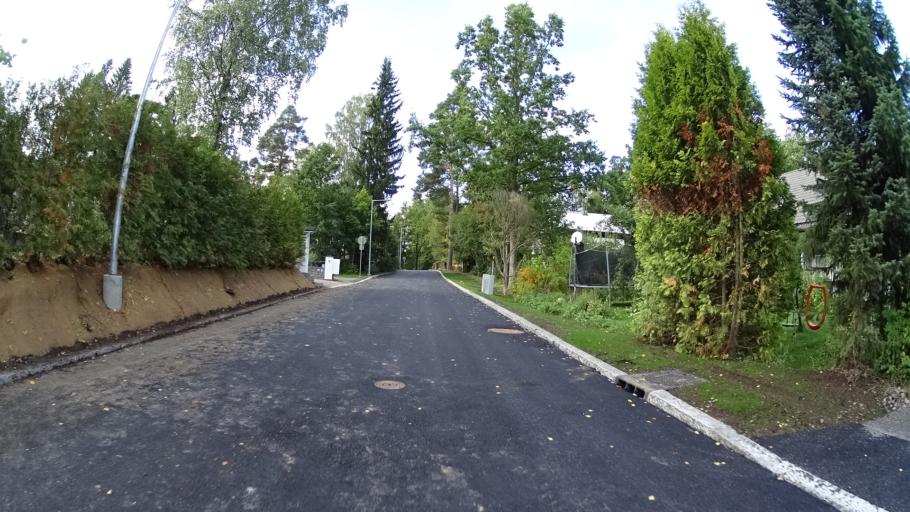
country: FI
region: Uusimaa
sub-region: Helsinki
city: Kilo
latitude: 60.2453
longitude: 24.7540
